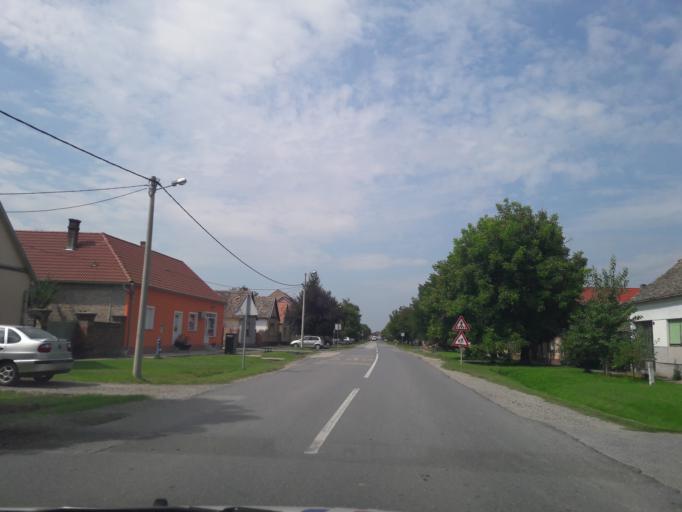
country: HR
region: Osjecko-Baranjska
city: Bizovac
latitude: 45.5099
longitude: 18.4680
